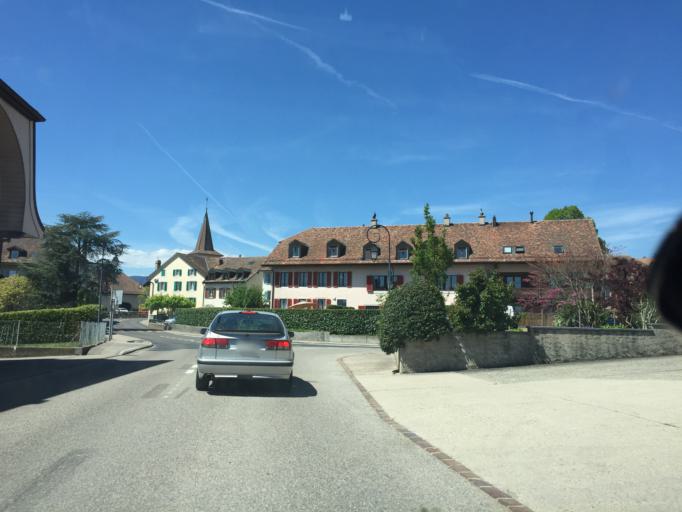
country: CH
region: Vaud
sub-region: Morges District
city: Aubonne
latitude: 46.5097
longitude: 6.4303
